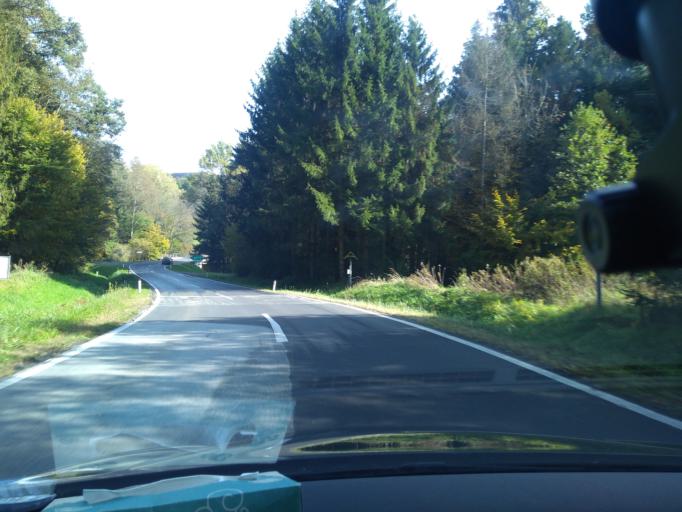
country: AT
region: Styria
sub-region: Politischer Bezirk Graz-Umgebung
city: Mellach
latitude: 46.9311
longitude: 15.5247
